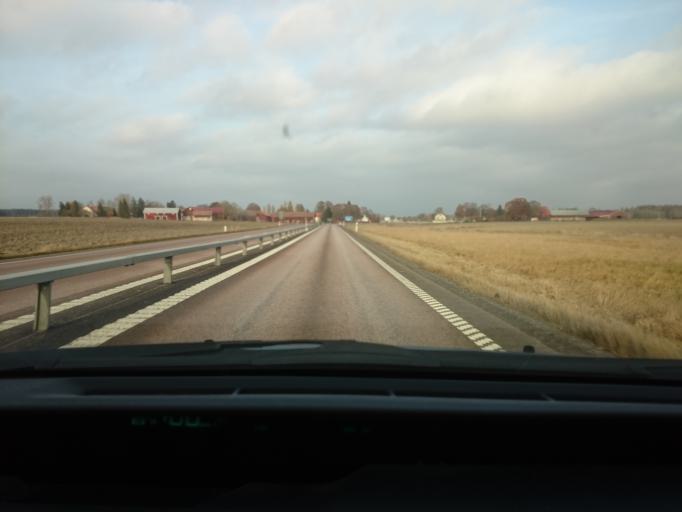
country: SE
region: Vaestmanland
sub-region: Sala Kommun
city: Sala
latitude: 59.8524
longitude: 16.5357
